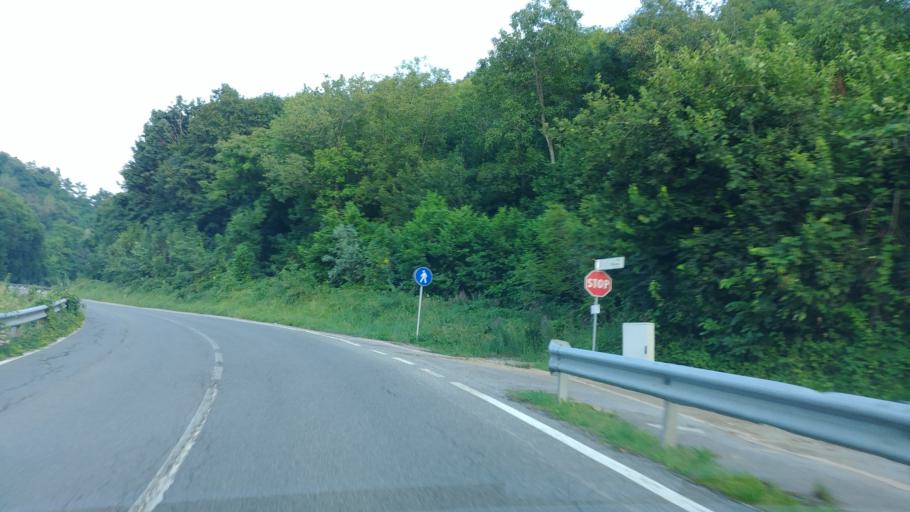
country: IT
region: Piedmont
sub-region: Provincia di Cuneo
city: Peveragno
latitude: 44.3329
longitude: 7.6069
